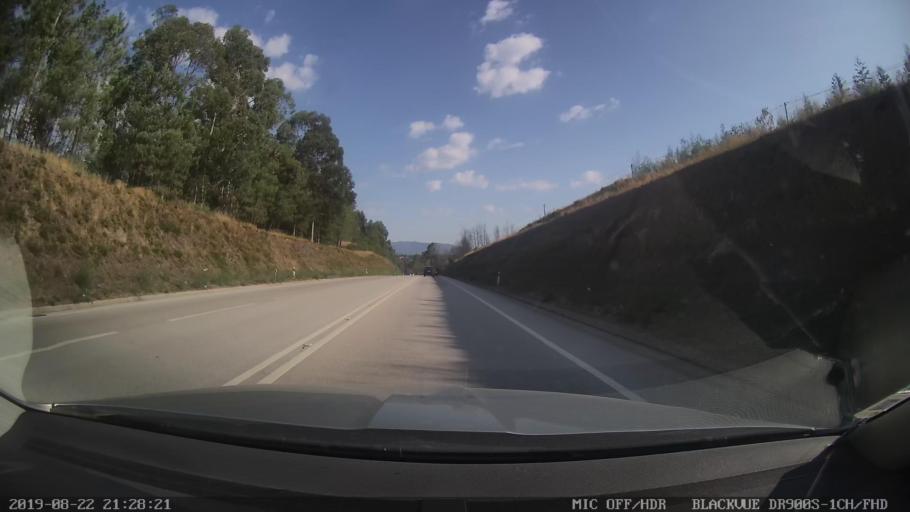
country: PT
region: Leiria
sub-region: Pedrogao Grande
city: Pedrogao Grande
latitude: 39.8908
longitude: -8.1210
